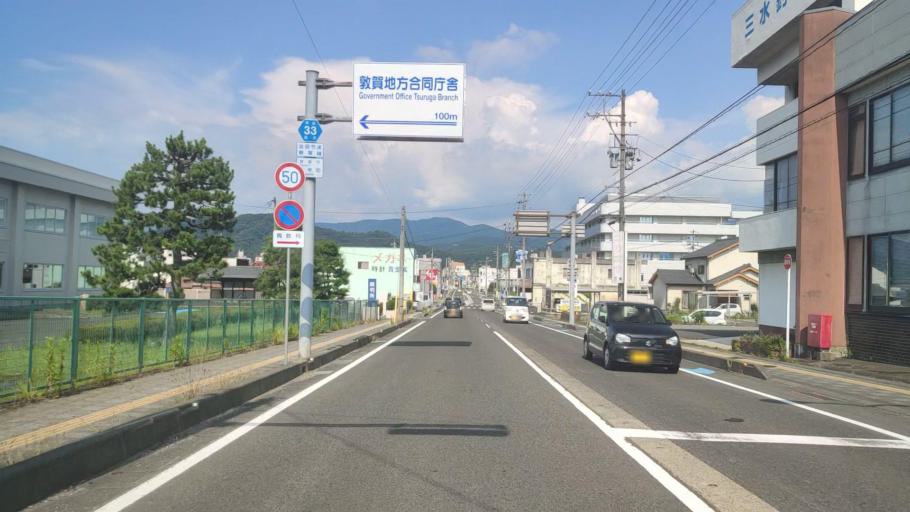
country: JP
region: Fukui
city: Tsuruga
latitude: 35.6528
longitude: 136.0620
